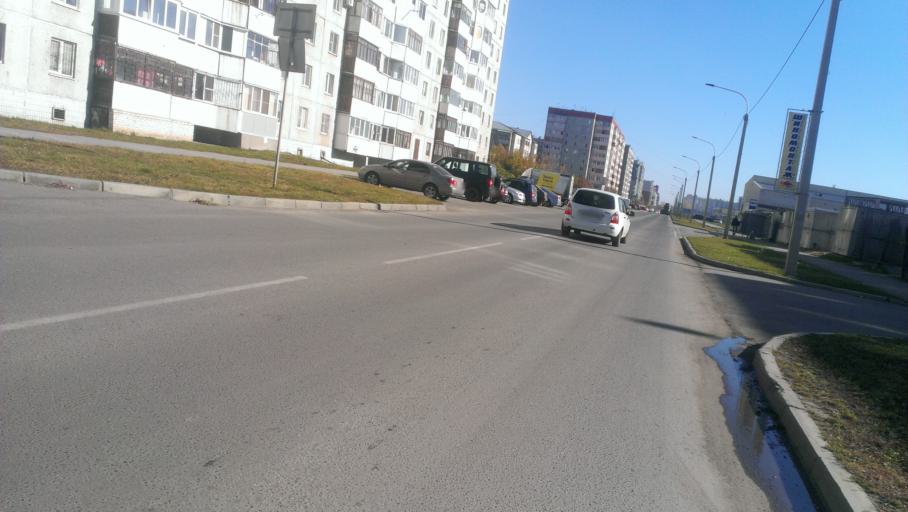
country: RU
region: Altai Krai
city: Novosilikatnyy
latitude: 53.3308
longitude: 83.6559
